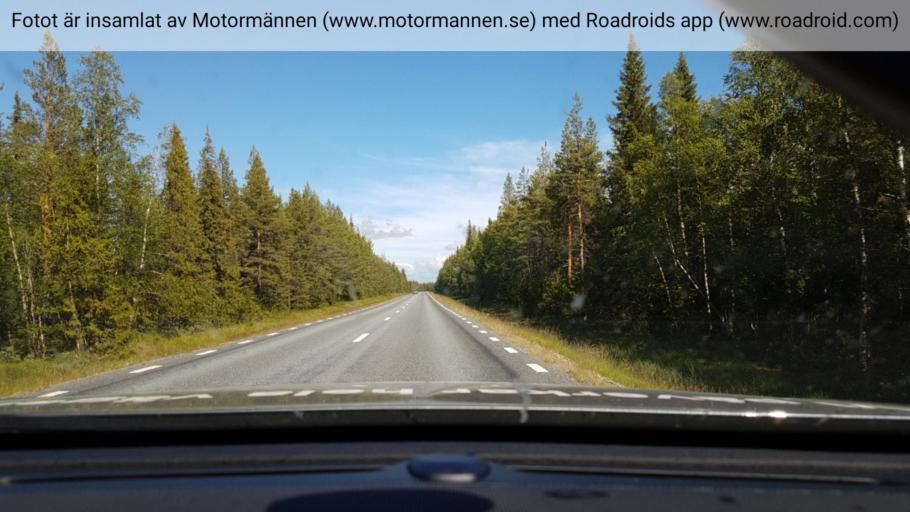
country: SE
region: Vaesterbotten
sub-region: Sorsele Kommun
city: Sorsele
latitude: 65.5678
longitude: 18.0117
